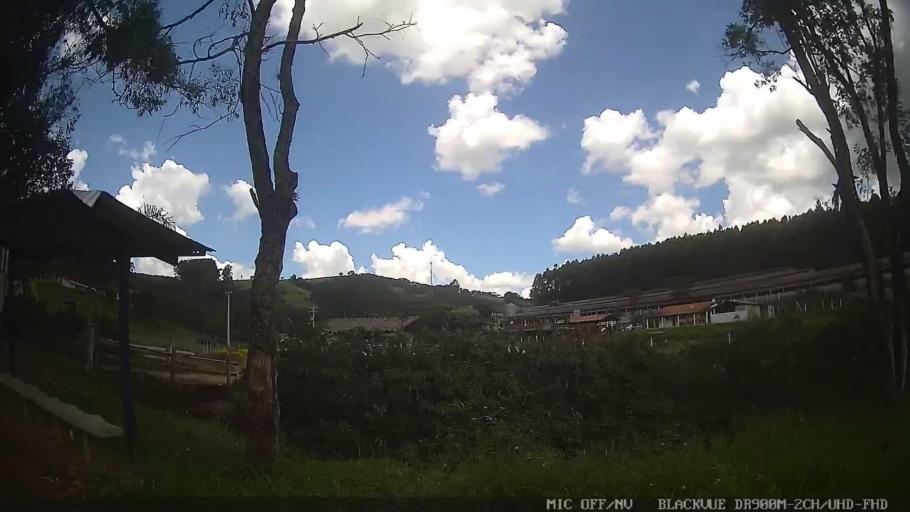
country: BR
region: Sao Paulo
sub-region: Braganca Paulista
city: Braganca Paulista
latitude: -22.9965
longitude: -46.4874
